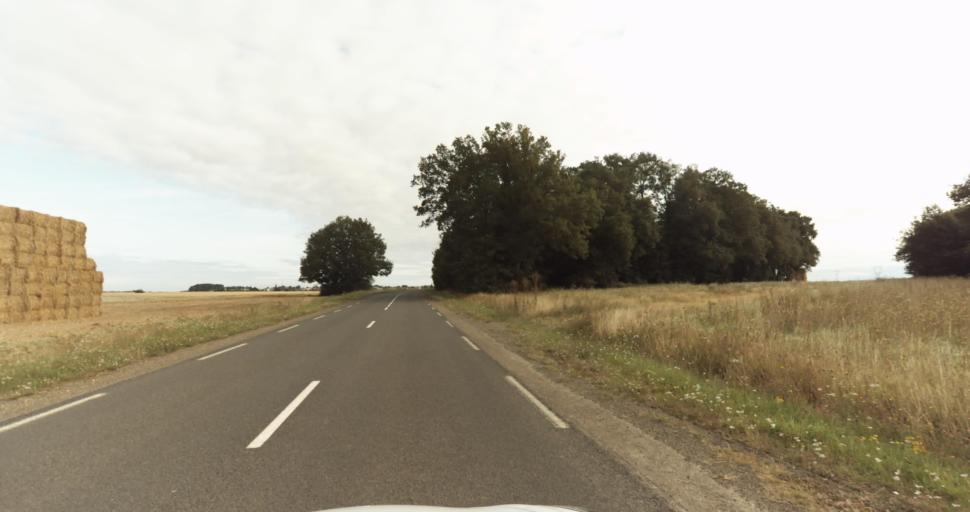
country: FR
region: Haute-Normandie
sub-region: Departement de l'Eure
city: La Madeleine-de-Nonancourt
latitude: 48.8483
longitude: 1.2413
